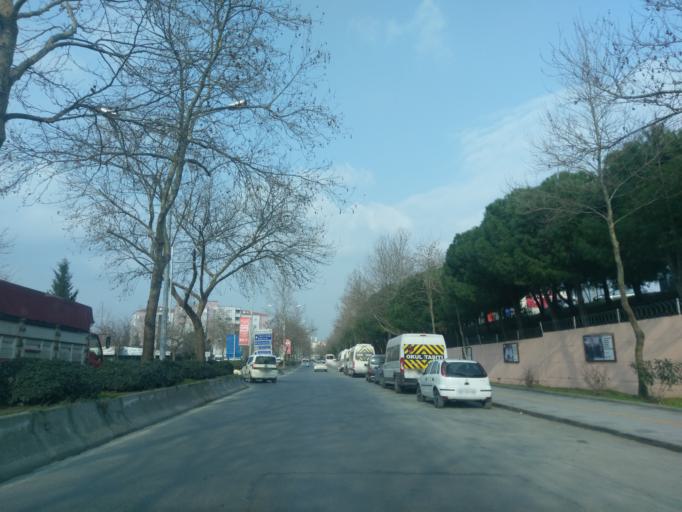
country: TR
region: Istanbul
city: Silivri
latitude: 41.0771
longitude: 28.2541
